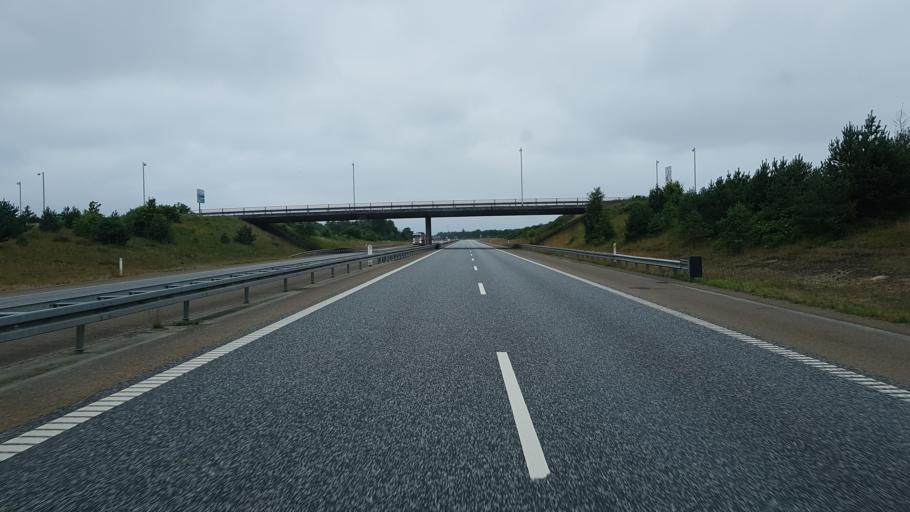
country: DK
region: Central Jutland
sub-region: Ikast-Brande Kommune
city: Brande
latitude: 55.9656
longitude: 9.1002
